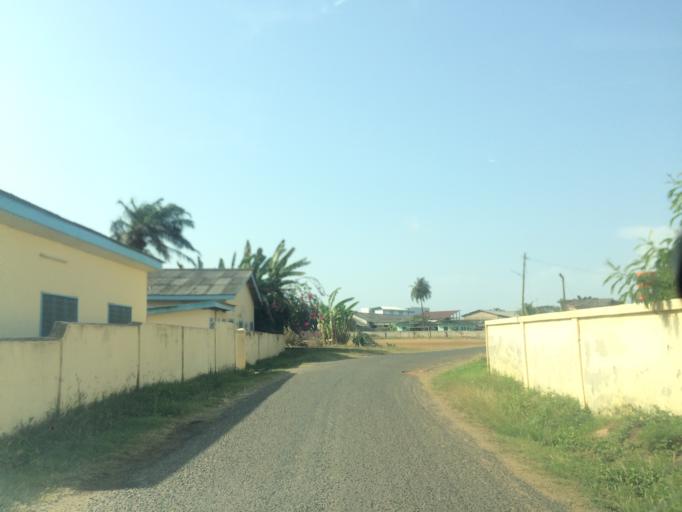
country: GH
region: Greater Accra
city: Accra
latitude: 5.5577
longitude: -0.1701
